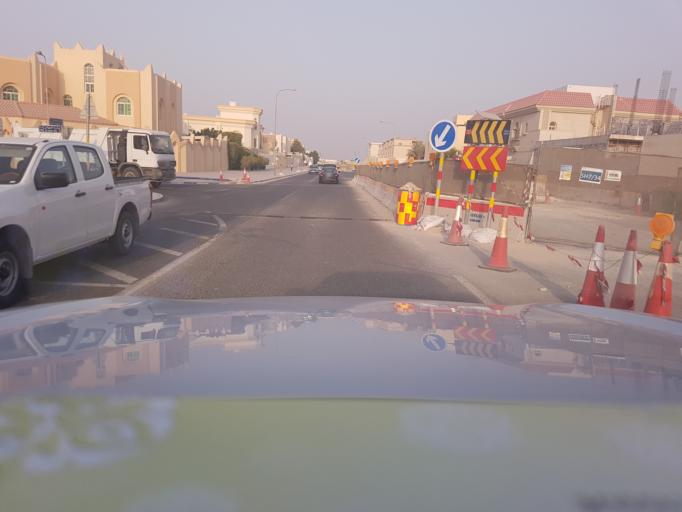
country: QA
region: Baladiyat ad Dawhah
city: Doha
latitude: 25.2320
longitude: 51.5612
